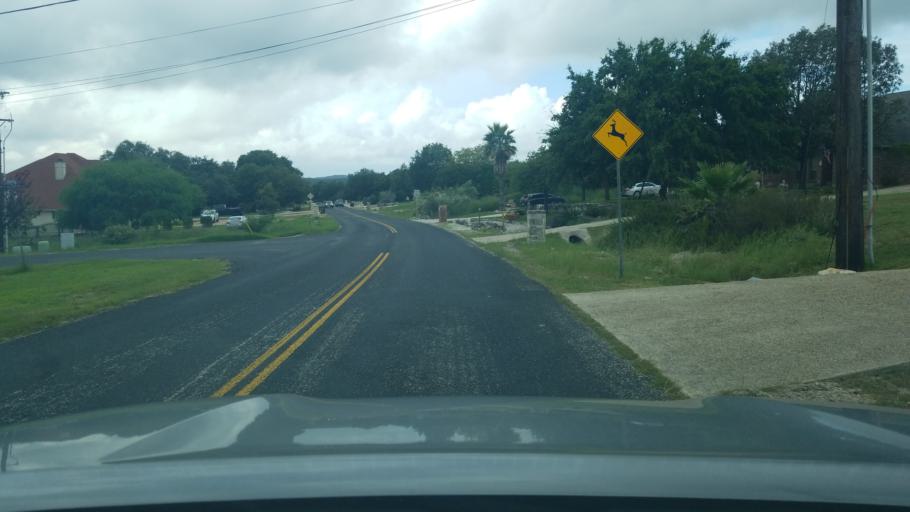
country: US
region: Texas
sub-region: Bexar County
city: Timberwood Park
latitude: 29.6840
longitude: -98.5164
